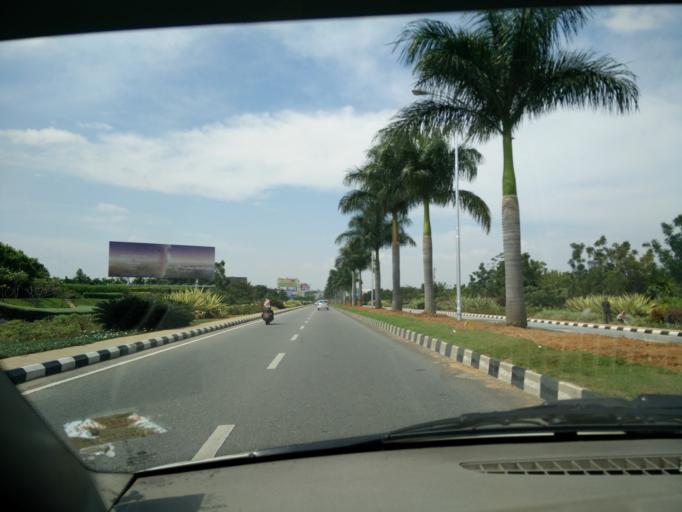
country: IN
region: Karnataka
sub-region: Bangalore Rural
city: Devanhalli
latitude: 13.1980
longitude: 77.6854
